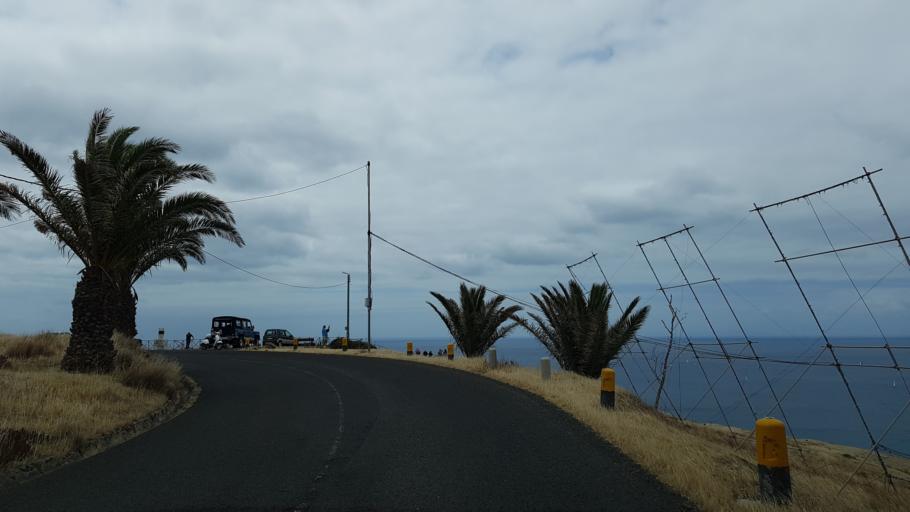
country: PT
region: Madeira
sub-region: Porto Santo
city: Vila de Porto Santo
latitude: 33.0670
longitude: -16.3176
